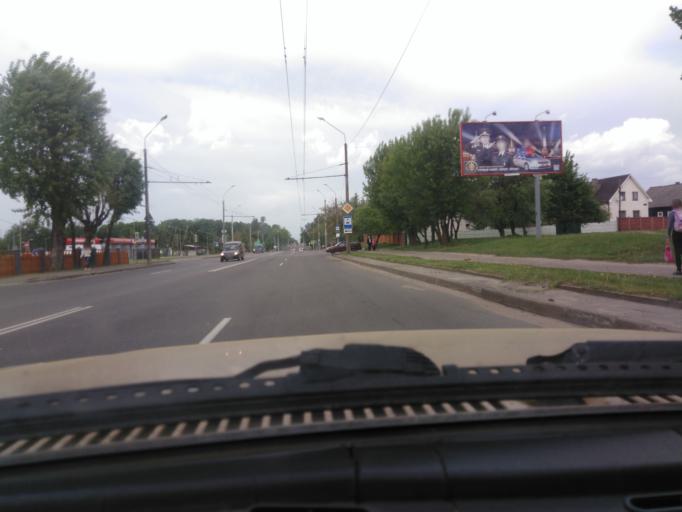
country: BY
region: Mogilev
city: Mahilyow
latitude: 53.9330
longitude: 30.3362
